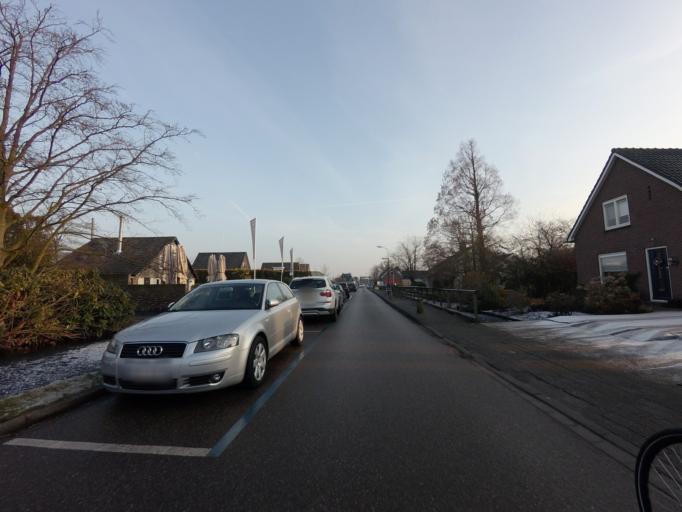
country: NL
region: Utrecht
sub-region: Gemeente De Ronde Venen
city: Mijdrecht
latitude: 52.2251
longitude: 4.9263
